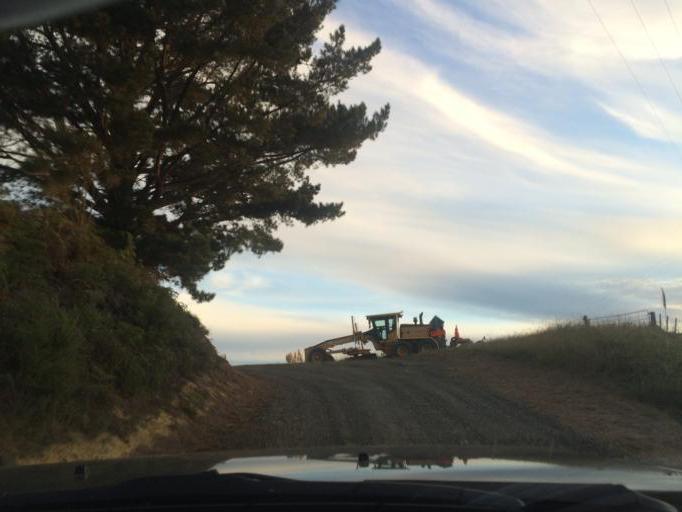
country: NZ
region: Northland
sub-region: Whangarei
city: Maungatapere
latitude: -35.8059
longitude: 174.0417
